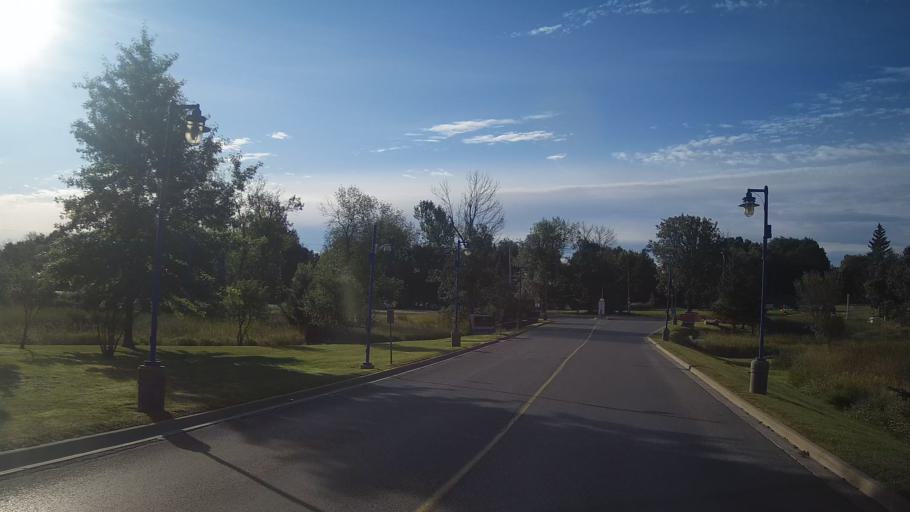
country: CA
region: Ontario
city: Gananoque
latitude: 44.3416
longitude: -76.1405
